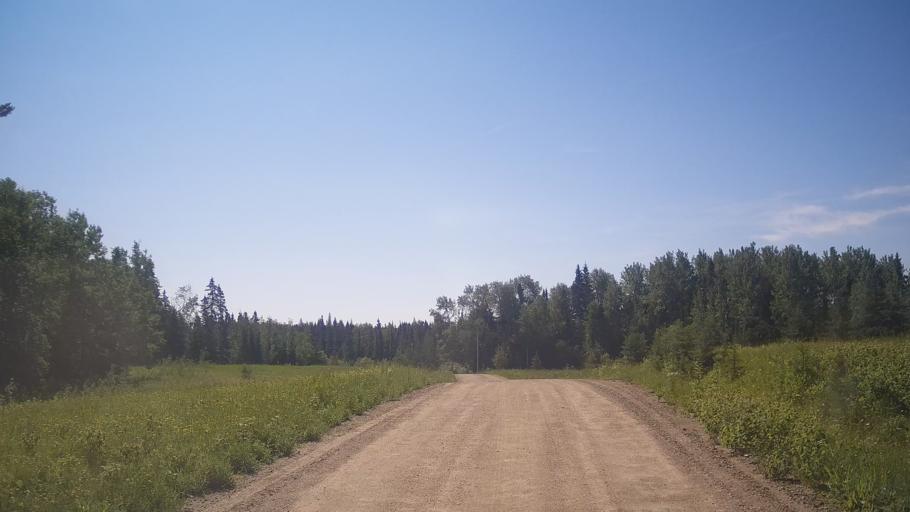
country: CA
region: Ontario
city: Dryden
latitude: 49.8204
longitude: -93.3375
